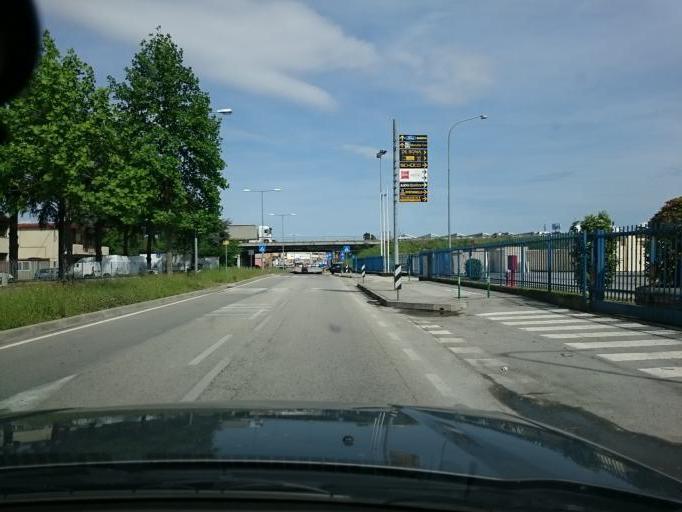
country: IT
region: Veneto
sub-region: Provincia di Padova
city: Noventa
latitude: 45.4086
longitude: 11.9309
